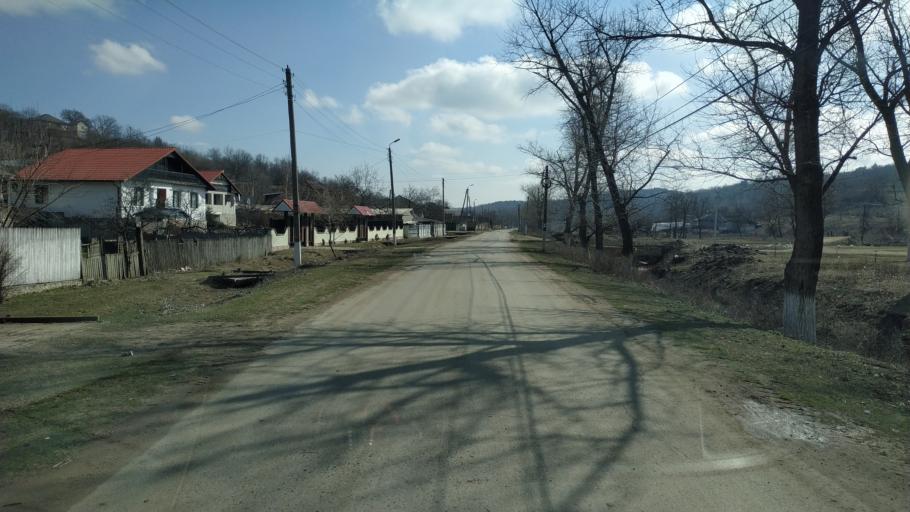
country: MD
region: Hincesti
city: Hincesti
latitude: 46.8782
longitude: 28.6273
